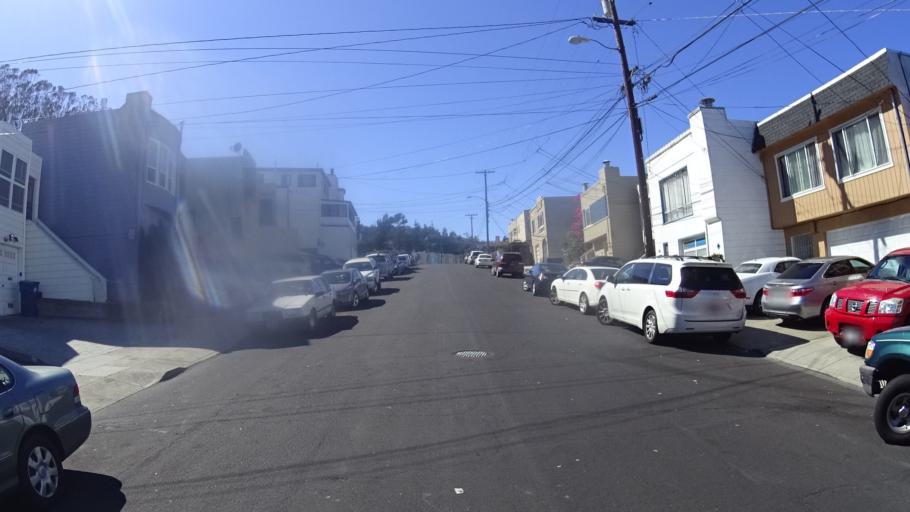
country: US
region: California
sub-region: San Mateo County
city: Daly City
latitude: 37.7032
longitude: -122.4553
